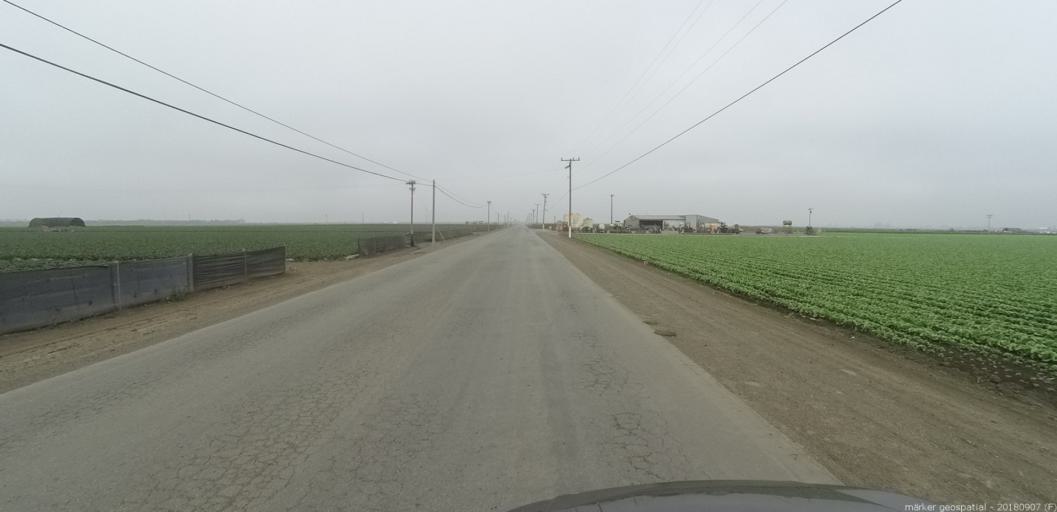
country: US
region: California
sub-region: Monterey County
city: Castroville
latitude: 36.7272
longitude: -121.7501
